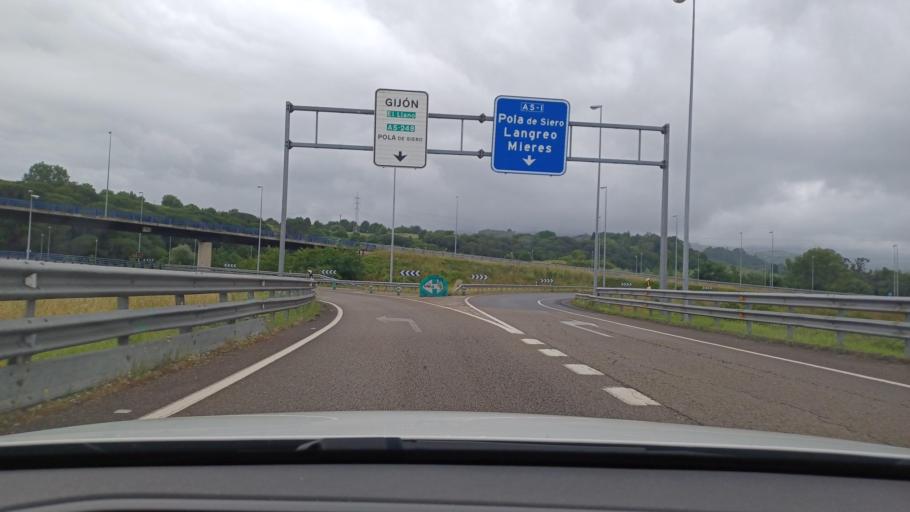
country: ES
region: Asturias
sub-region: Province of Asturias
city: Gijon
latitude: 43.5150
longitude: -5.6573
